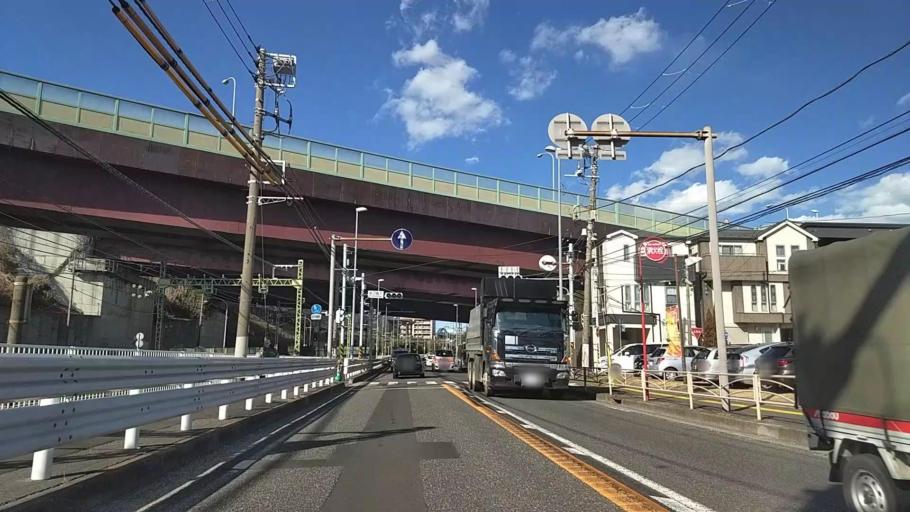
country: JP
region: Kanagawa
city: Zushi
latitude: 35.3555
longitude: 139.6281
